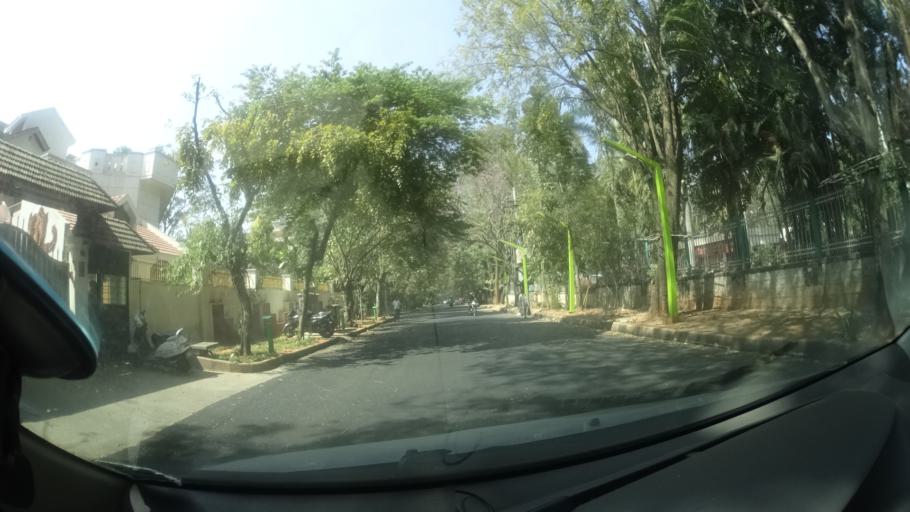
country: IN
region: Karnataka
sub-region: Bangalore Urban
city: Bangalore
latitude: 13.0115
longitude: 77.5826
